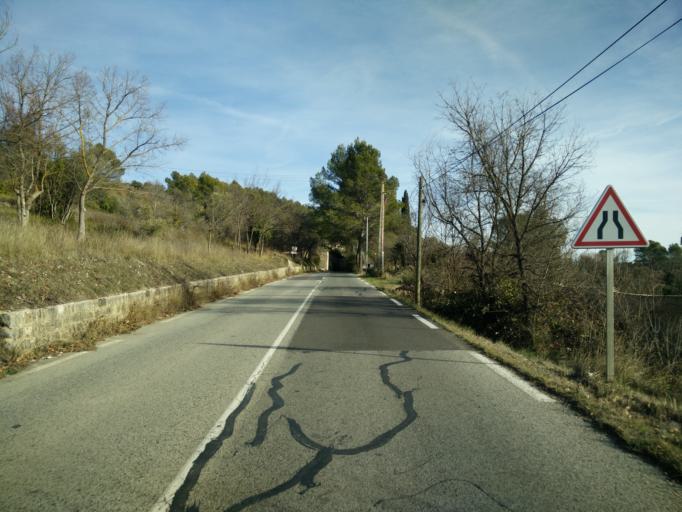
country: FR
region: Provence-Alpes-Cote d'Azur
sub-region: Departement du Var
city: Montauroux
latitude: 43.5972
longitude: 6.7916
